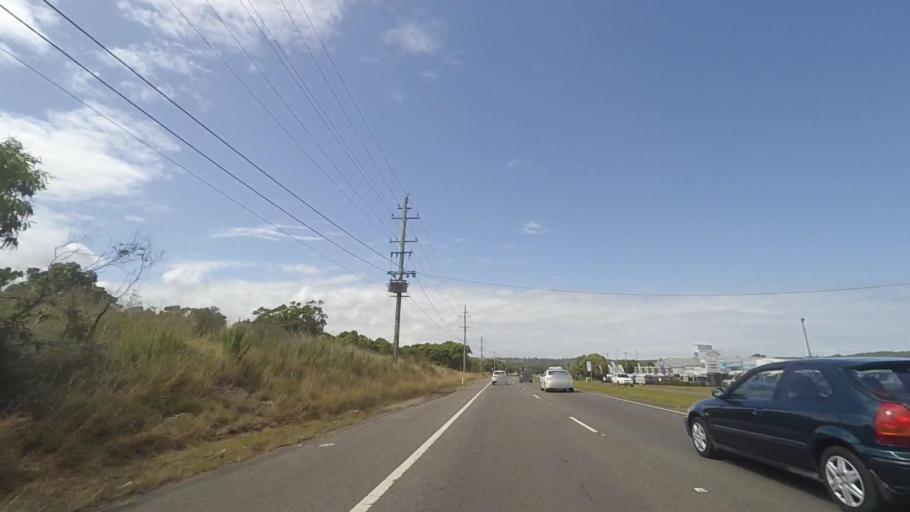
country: AU
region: New South Wales
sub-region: Lake Macquarie Shire
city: Windale
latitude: -32.9973
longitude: 151.6862
